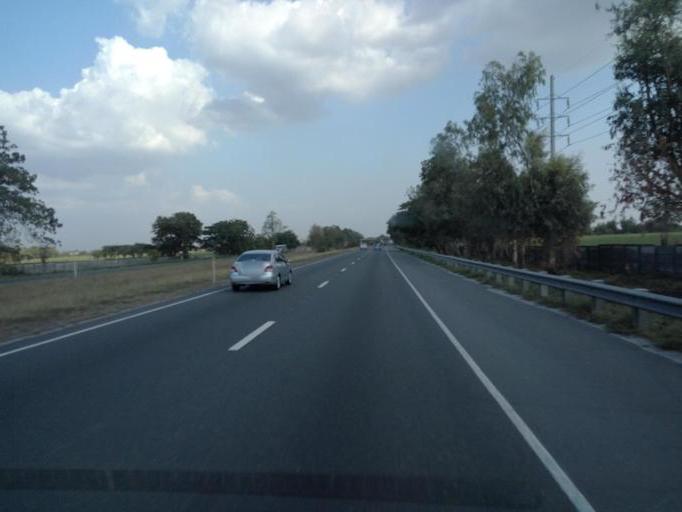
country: PH
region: Central Luzon
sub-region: Province of Pampanga
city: Acli
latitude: 15.1263
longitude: 120.6472
